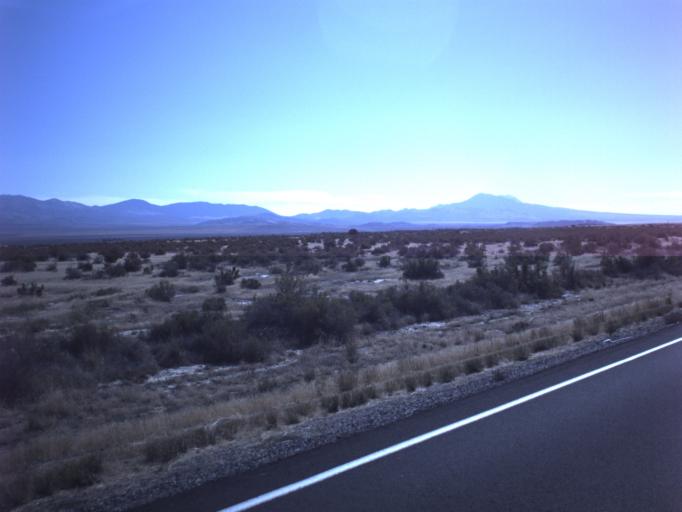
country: US
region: Utah
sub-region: Tooele County
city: Grantsville
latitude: 40.2641
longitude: -112.7410
